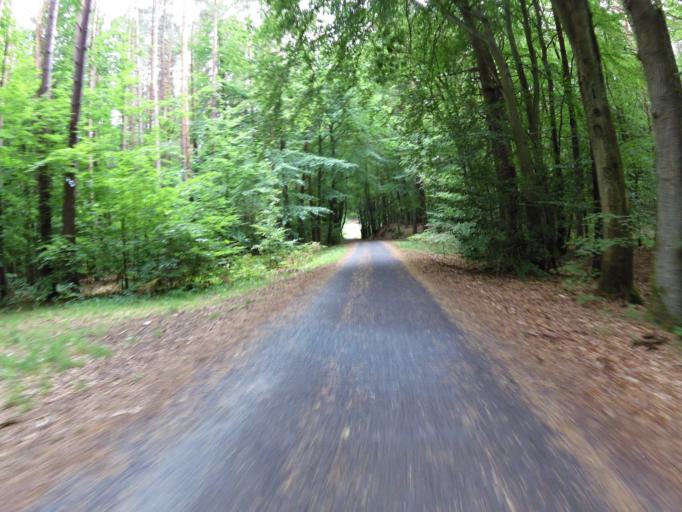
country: DE
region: Mecklenburg-Vorpommern
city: Seebad Heringsdorf
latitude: 53.9276
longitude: 14.1729
